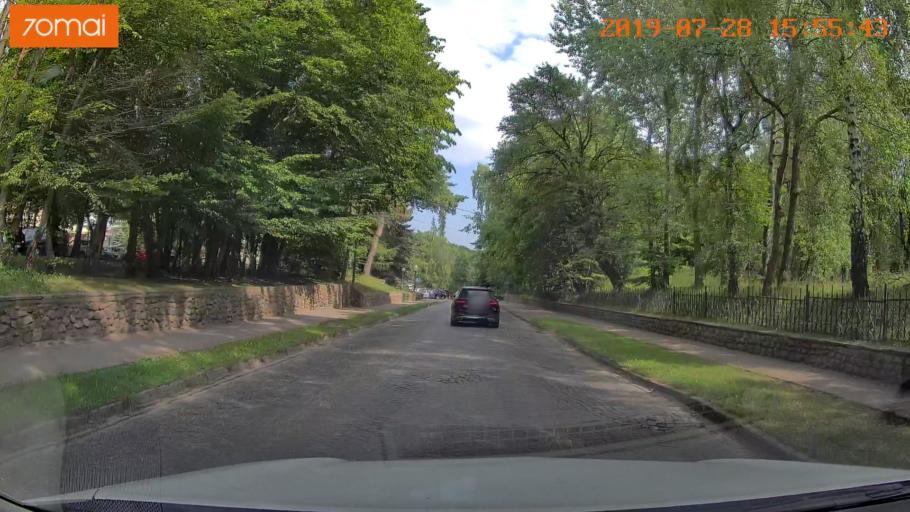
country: RU
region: Kaliningrad
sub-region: Gorod Svetlogorsk
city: Svetlogorsk
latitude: 54.9407
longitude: 20.1415
